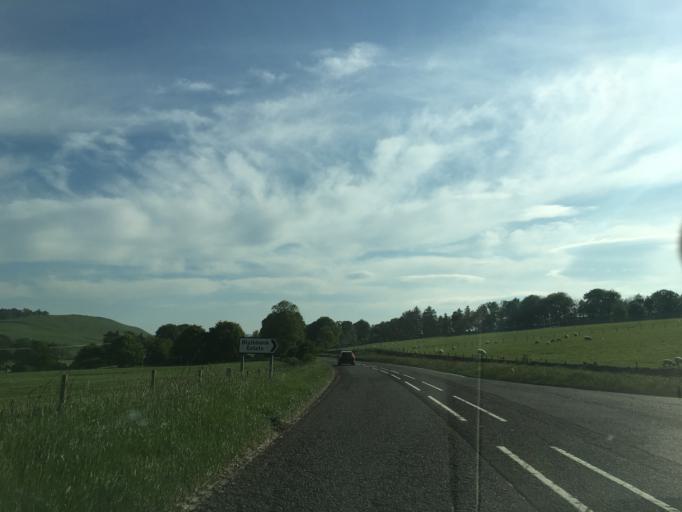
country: GB
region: Scotland
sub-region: The Scottish Borders
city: West Linton
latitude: 55.7115
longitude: -3.3498
